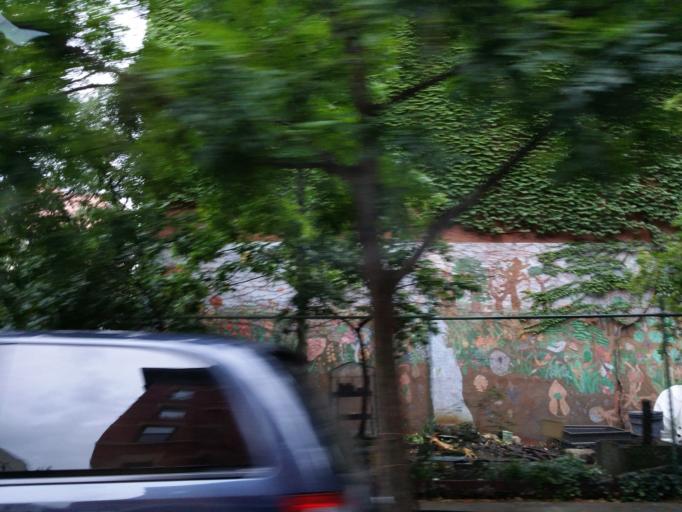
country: US
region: New York
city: New York City
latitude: 40.7283
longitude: -73.9793
